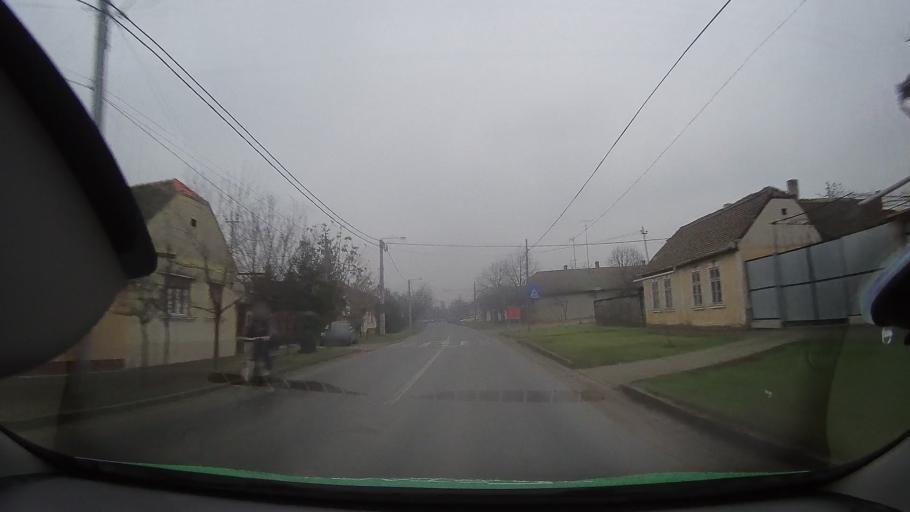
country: RO
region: Bihor
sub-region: Municipiul Salonta
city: Salonta
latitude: 46.7963
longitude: 21.6588
